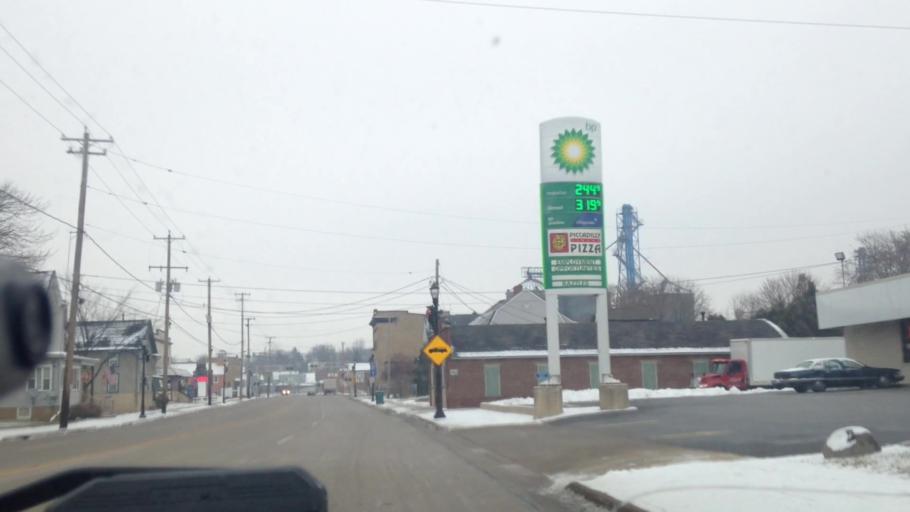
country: US
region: Wisconsin
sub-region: Washington County
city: Slinger
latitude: 43.4206
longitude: -88.3447
